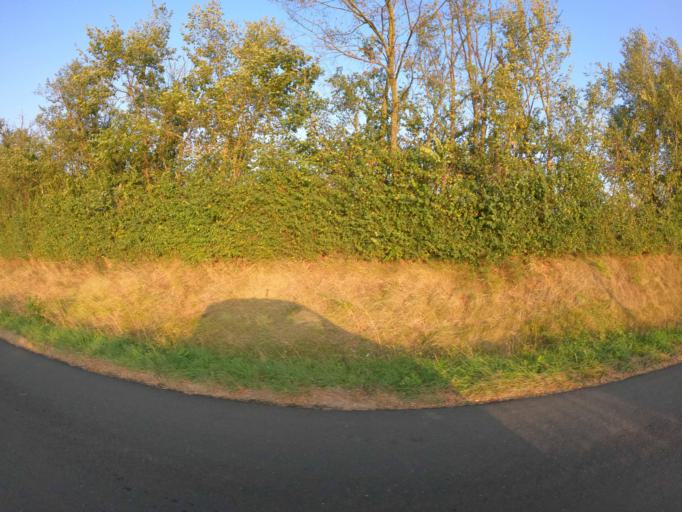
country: FR
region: Pays de la Loire
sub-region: Departement de la Sarthe
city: Brulon
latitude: 47.9302
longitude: -0.2287
